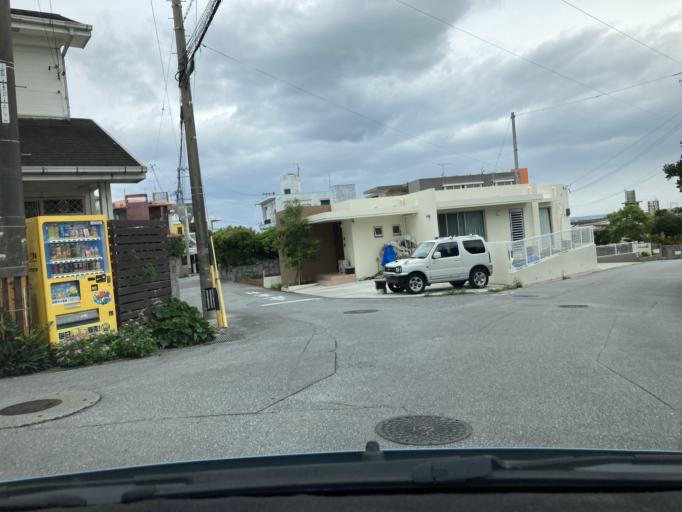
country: JP
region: Okinawa
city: Itoman
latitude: 26.1430
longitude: 127.6793
